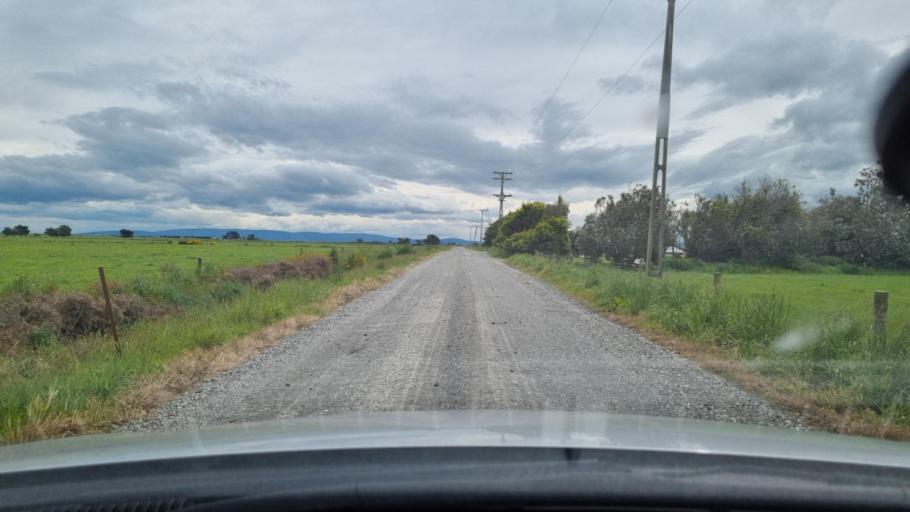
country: NZ
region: Southland
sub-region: Invercargill City
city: Invercargill
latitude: -46.4045
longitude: 168.2881
